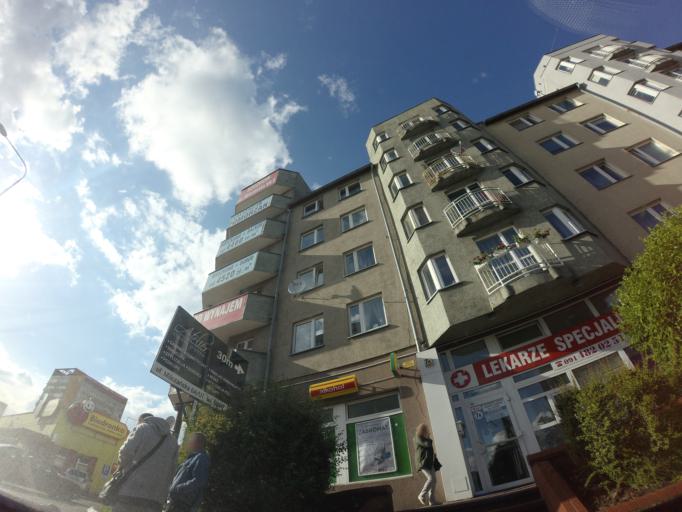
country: PL
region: West Pomeranian Voivodeship
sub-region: Szczecin
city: Szczecin
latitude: 53.4081
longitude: 14.5270
